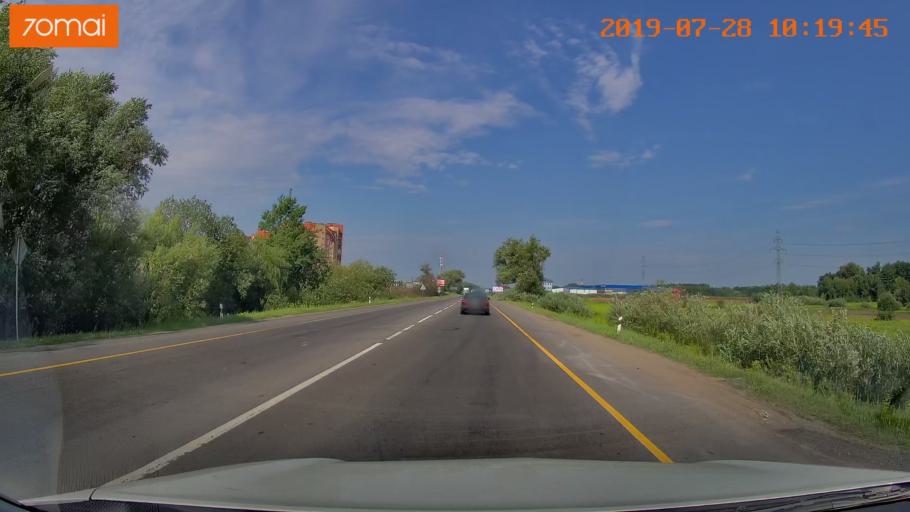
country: RU
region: Kaliningrad
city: Maloye Isakovo
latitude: 54.7483
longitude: 20.5839
